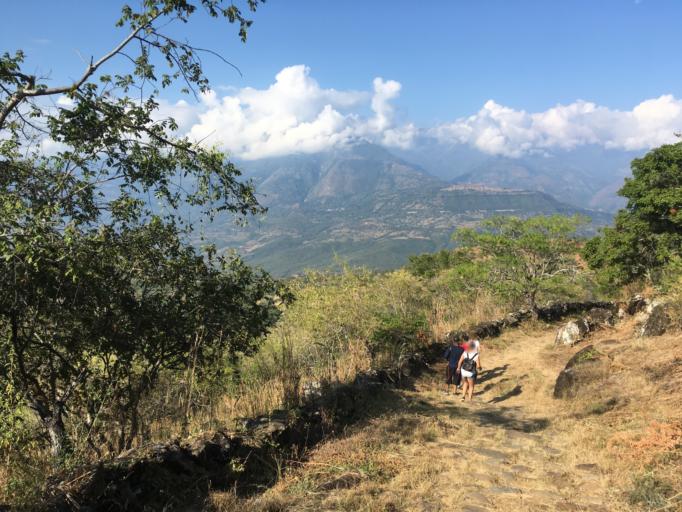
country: CO
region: Santander
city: Barichara
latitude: 6.6522
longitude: -73.2293
